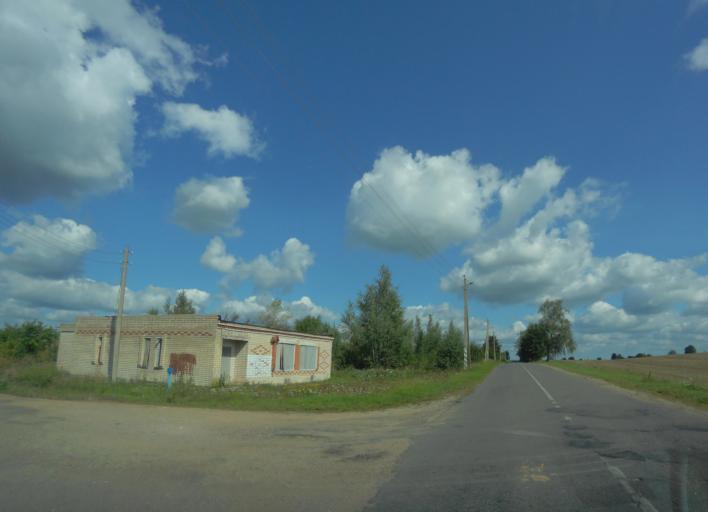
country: BY
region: Minsk
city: Zyembin
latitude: 54.4029
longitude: 28.3962
